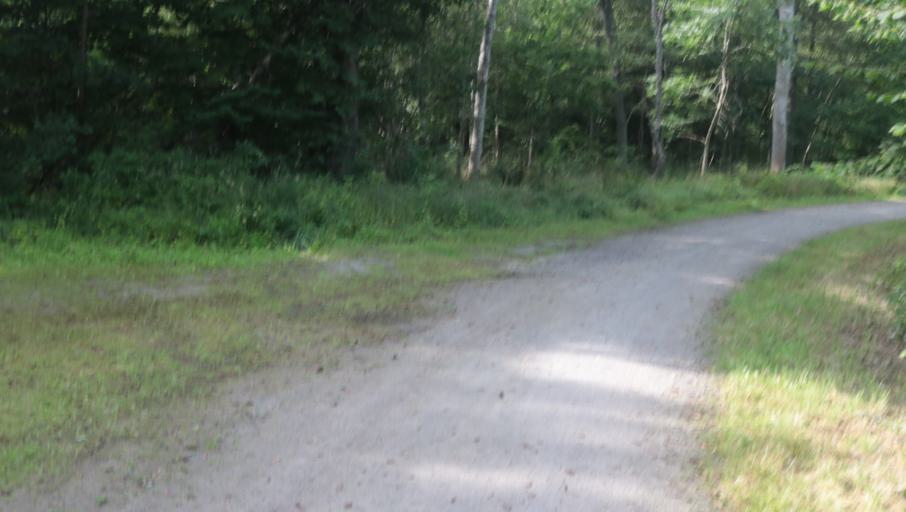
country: SE
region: Blekinge
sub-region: Karlshamns Kommun
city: Karlshamn
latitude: 56.2020
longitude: 14.8609
